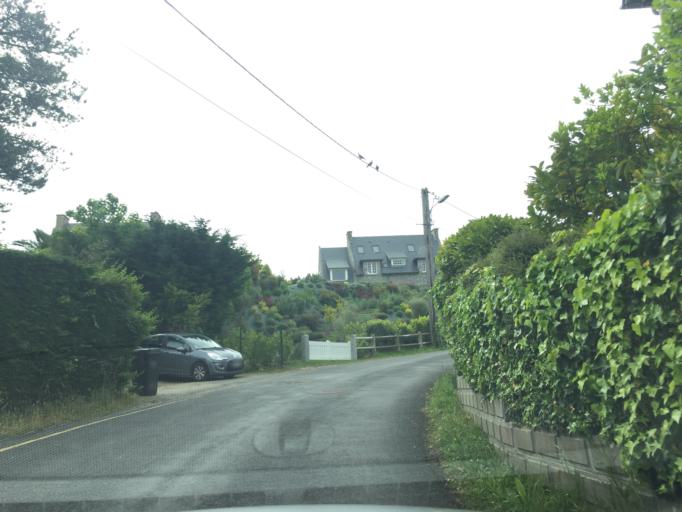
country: FR
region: Brittany
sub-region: Departement des Cotes-d'Armor
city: Saint-Cast-le-Guildo
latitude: 48.6228
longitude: -2.2444
